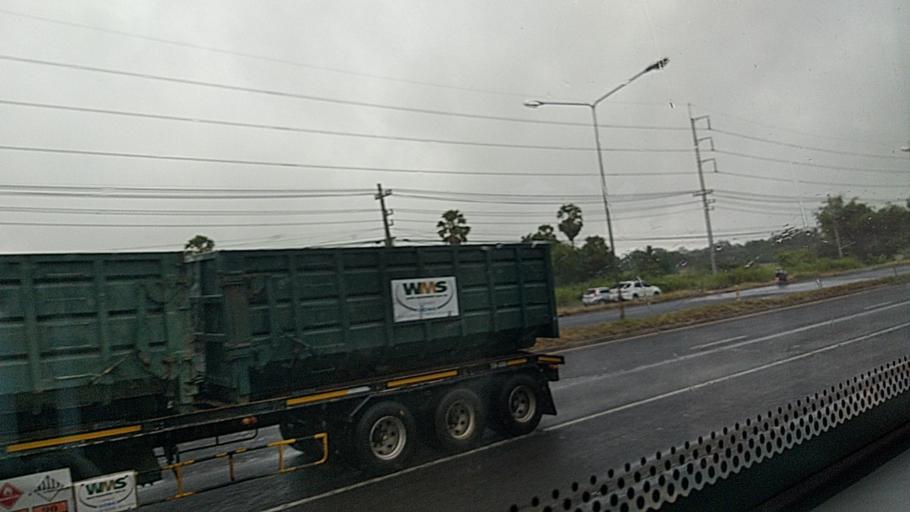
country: TH
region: Nakhon Ratchasima
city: Sikhio
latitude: 14.8698
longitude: 101.7567
